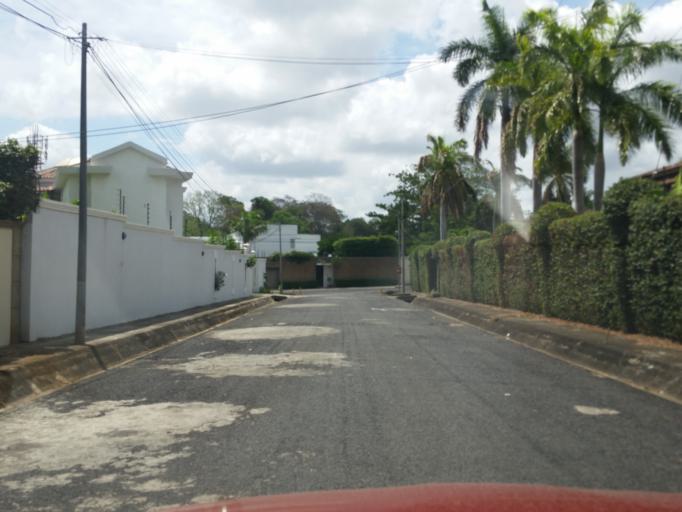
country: NI
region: Managua
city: Managua
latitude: 12.0783
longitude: -86.2402
